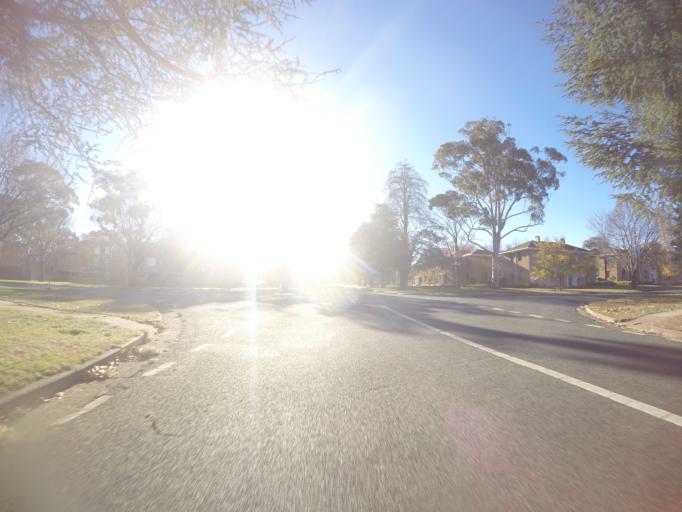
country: AU
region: Australian Capital Territory
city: Canberra
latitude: -35.2787
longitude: 149.1408
